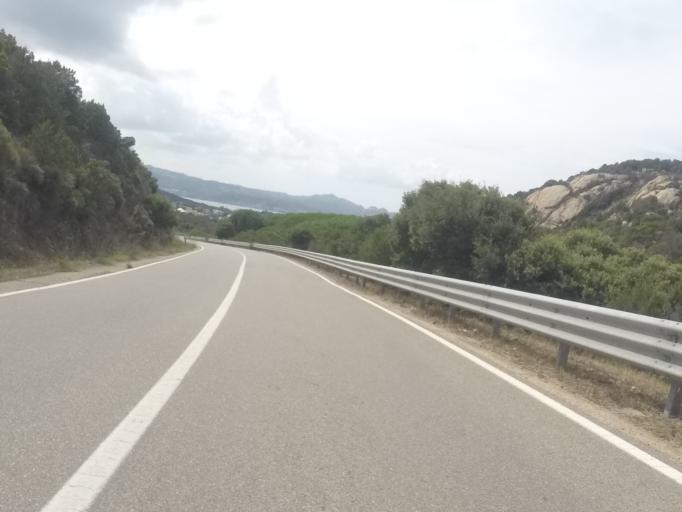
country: IT
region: Sardinia
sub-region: Provincia di Olbia-Tempio
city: Porto Cervo
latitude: 41.1335
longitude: 9.4883
